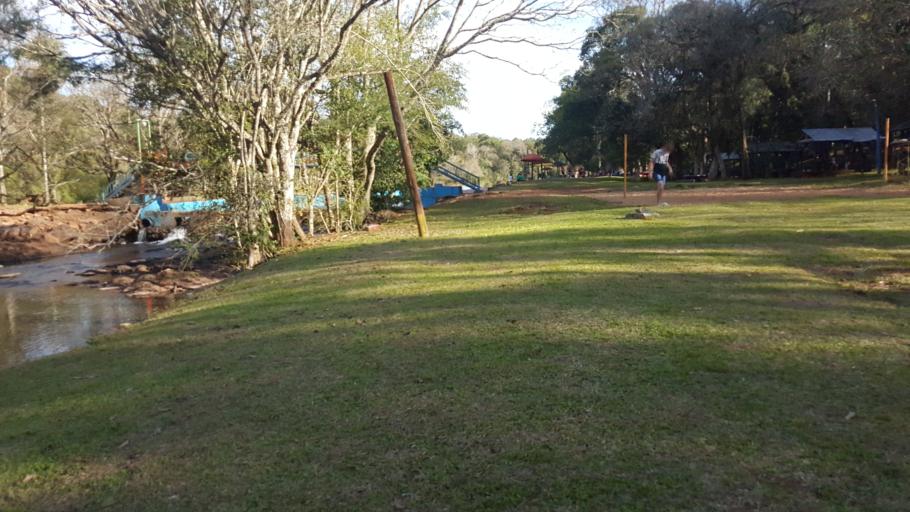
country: AR
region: Misiones
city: Puerto Leoni
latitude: -27.0002
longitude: -55.1782
